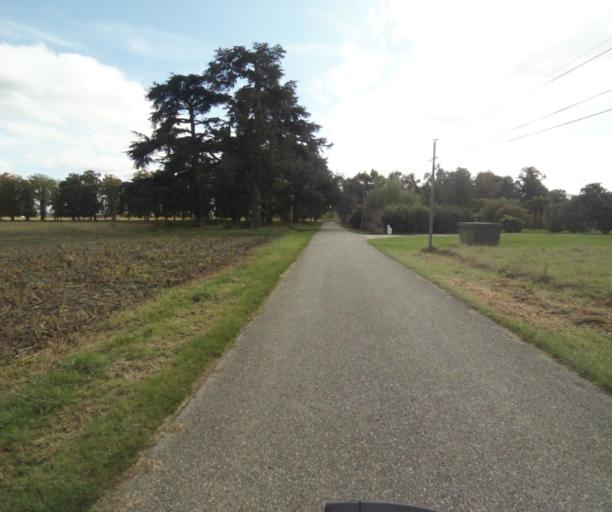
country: FR
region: Midi-Pyrenees
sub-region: Departement du Tarn-et-Garonne
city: Finhan
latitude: 43.9288
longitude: 1.2173
